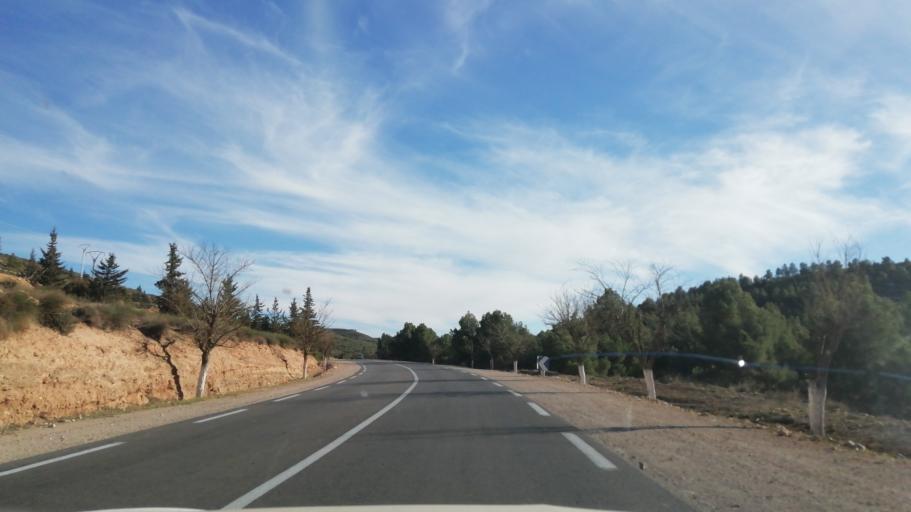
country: DZ
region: Tlemcen
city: Sebdou
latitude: 34.6054
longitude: -1.3279
